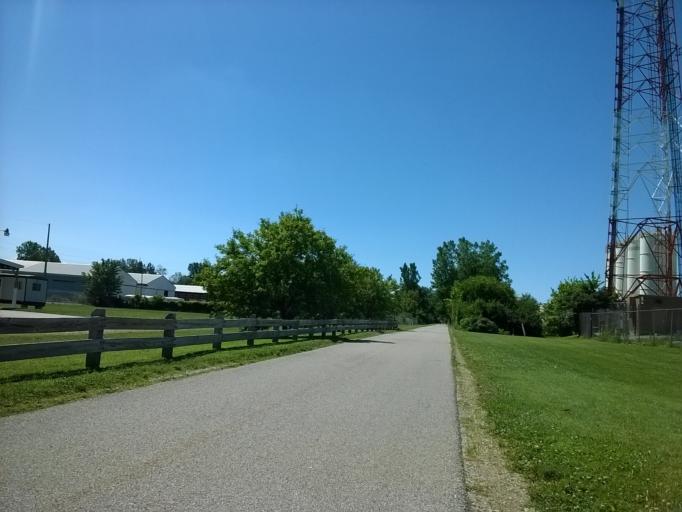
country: US
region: Indiana
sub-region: Hamilton County
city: Carmel
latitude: 39.9754
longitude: -86.1298
